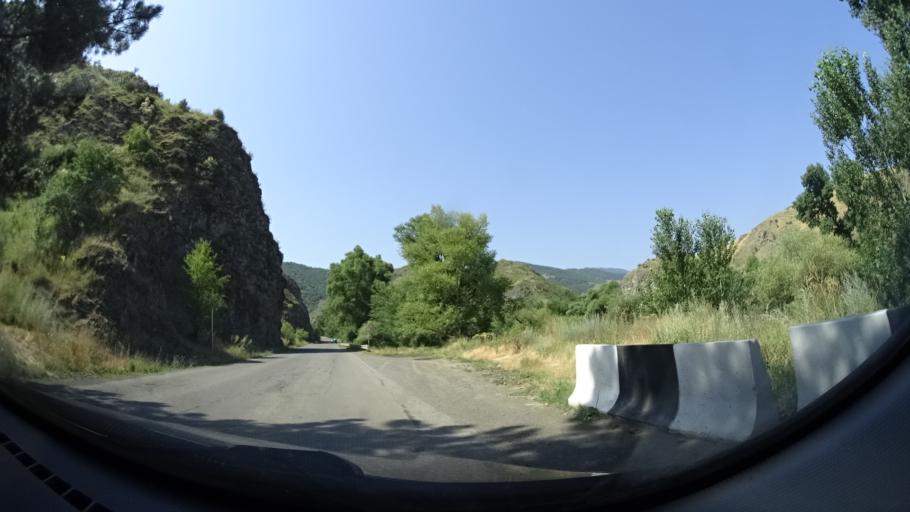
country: GE
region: Samtskhe-Javakheti
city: Akhaltsikhe
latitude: 41.6261
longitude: 43.0513
